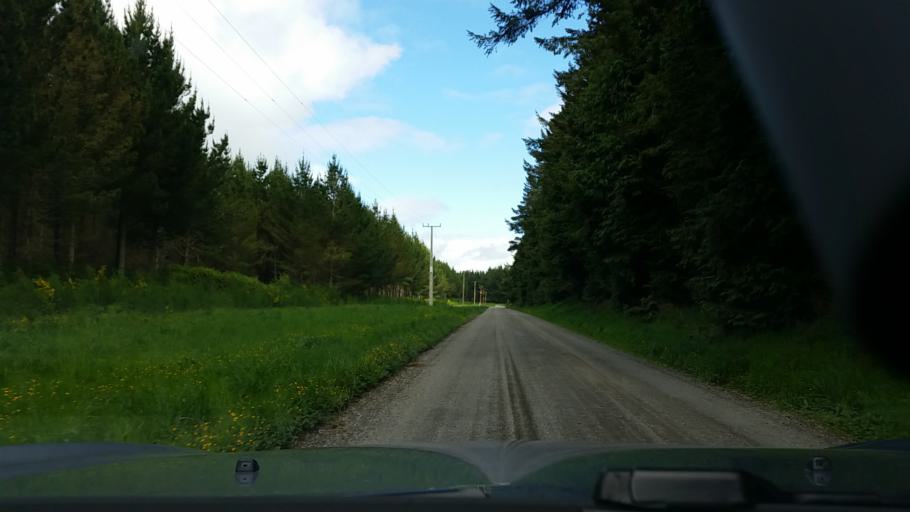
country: NZ
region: Bay of Plenty
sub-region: Whakatane District
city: Murupara
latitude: -38.3497
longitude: 176.5013
